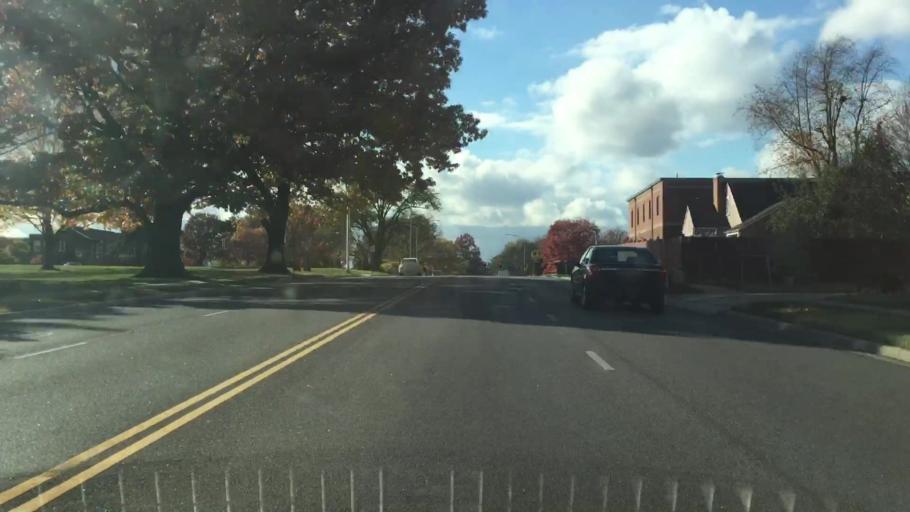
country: US
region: Kansas
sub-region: Johnson County
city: Mission
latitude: 39.0222
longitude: -94.6702
